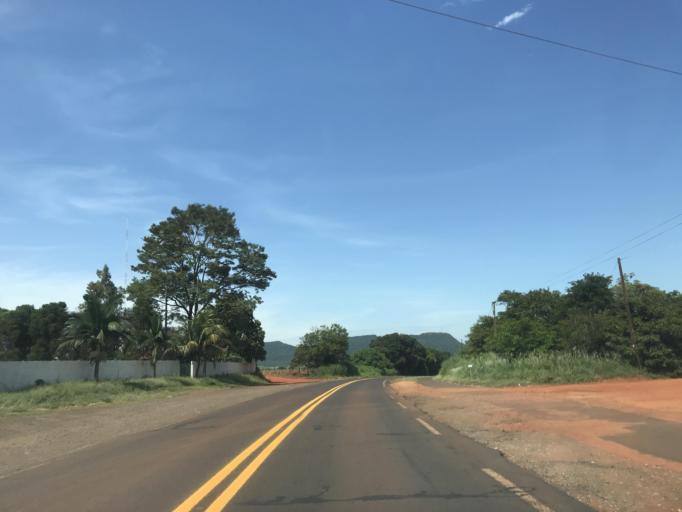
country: BR
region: Parana
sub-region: Terra Rica
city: Terra Rica
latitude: -22.7521
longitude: -52.6258
